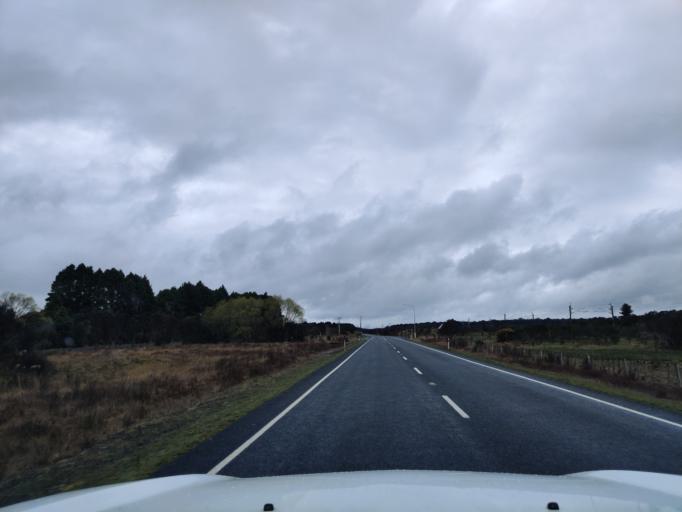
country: NZ
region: Manawatu-Wanganui
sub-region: Ruapehu District
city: Waiouru
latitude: -39.3423
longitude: 175.3779
